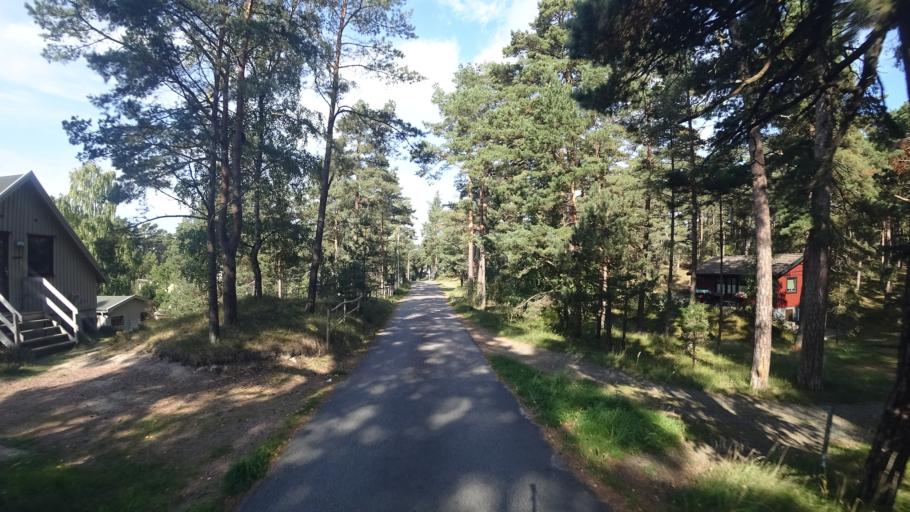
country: SE
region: Skane
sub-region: Kristianstads Kommun
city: Ahus
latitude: 55.9198
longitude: 14.3032
